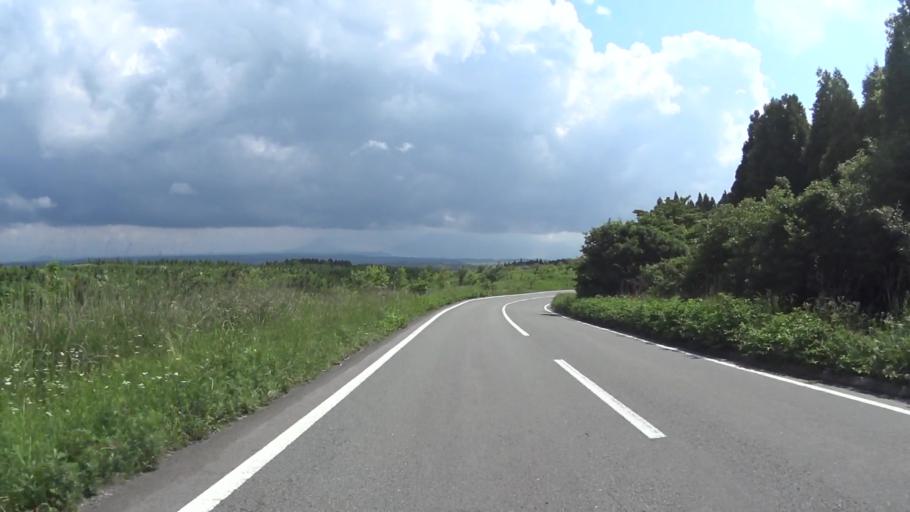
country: JP
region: Kumamoto
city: Aso
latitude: 33.0573
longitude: 131.1766
